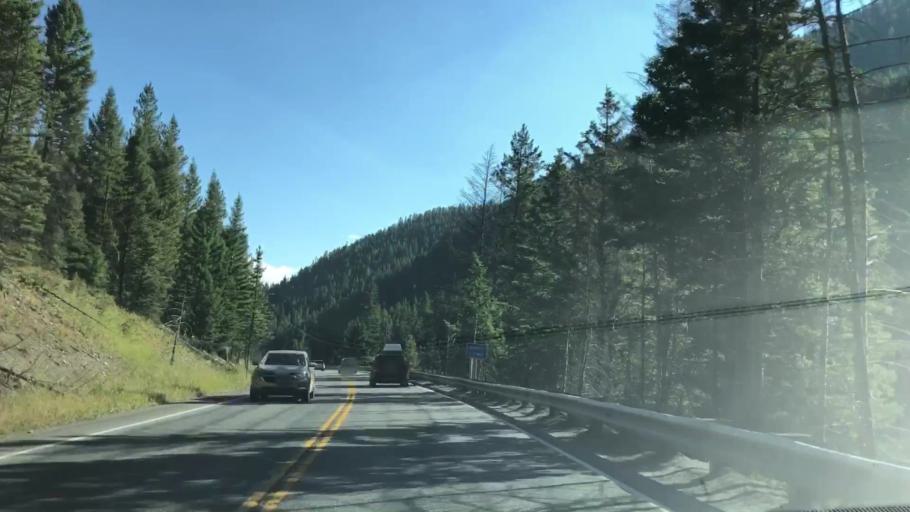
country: US
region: Montana
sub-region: Gallatin County
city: Big Sky
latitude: 45.3680
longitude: -111.1754
